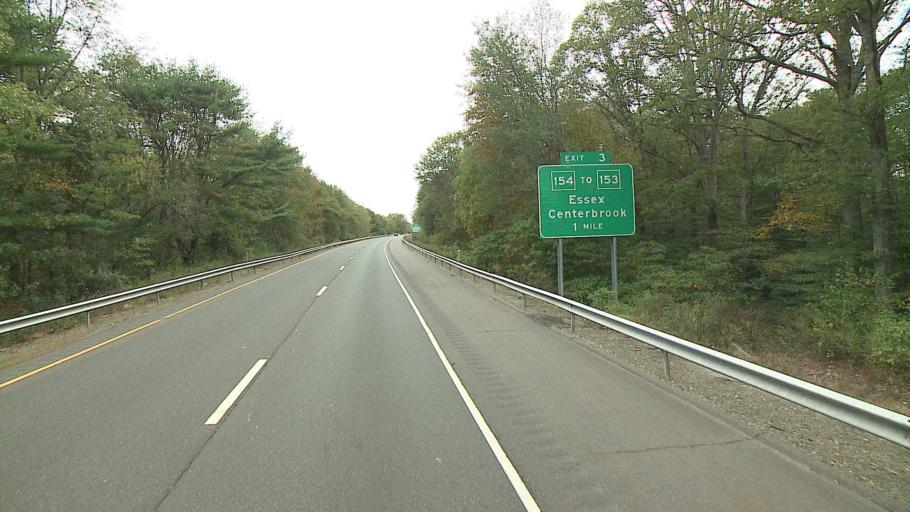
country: US
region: Connecticut
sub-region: Middlesex County
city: Essex Village
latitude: 41.3353
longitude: -72.3937
